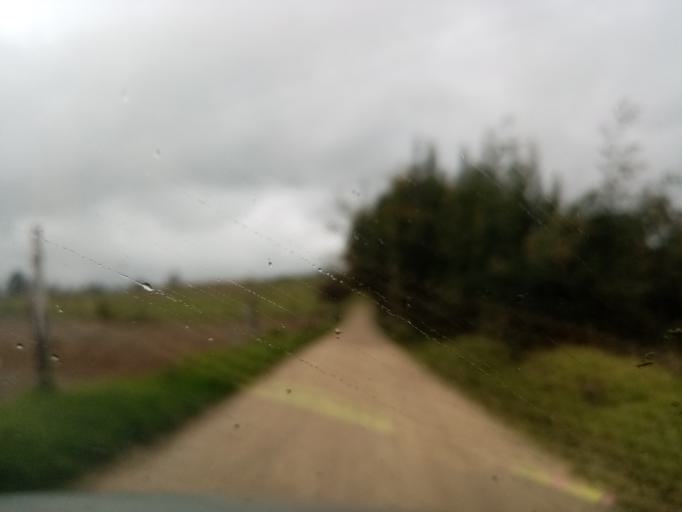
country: CO
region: Boyaca
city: Siachoque
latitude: 5.5606
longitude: -73.2501
